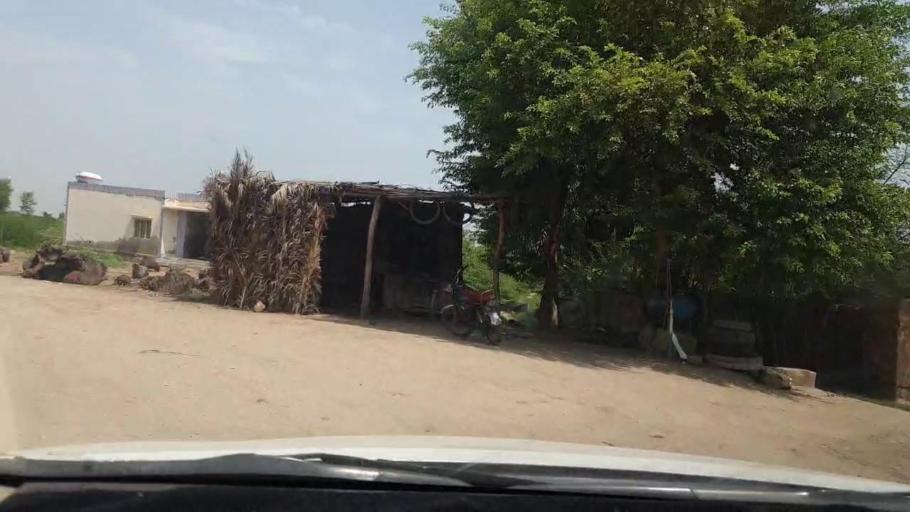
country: PK
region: Sindh
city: Rohri
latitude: 27.4973
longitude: 69.0236
